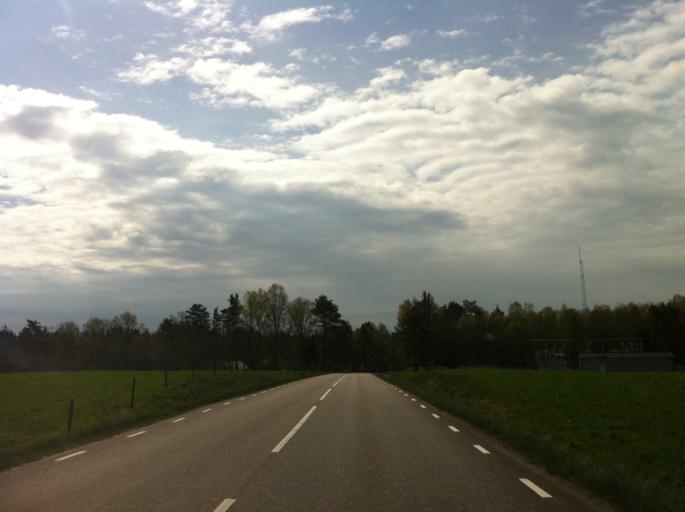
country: SE
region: Vaestra Goetaland
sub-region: Marks Kommun
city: Horred
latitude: 57.1477
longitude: 12.7278
